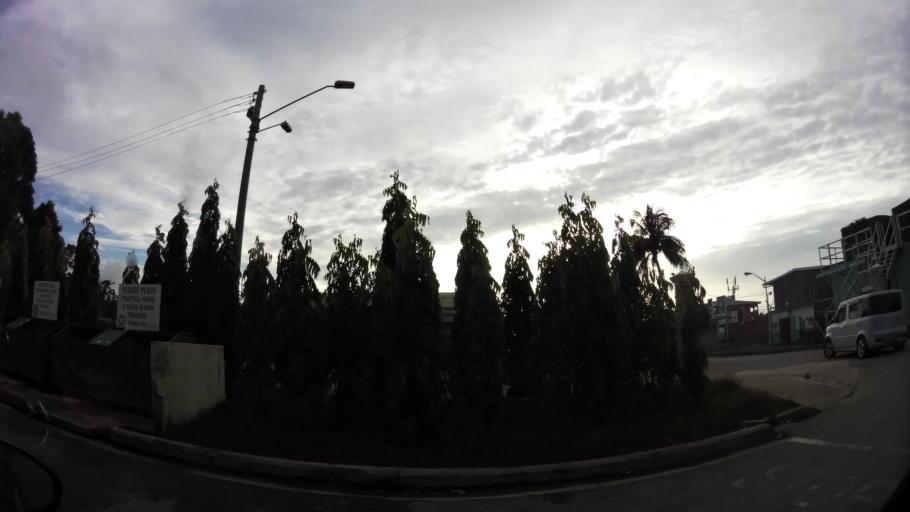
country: TT
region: Tunapuna/Piarco
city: Tunapuna
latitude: 10.6388
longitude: -61.4118
